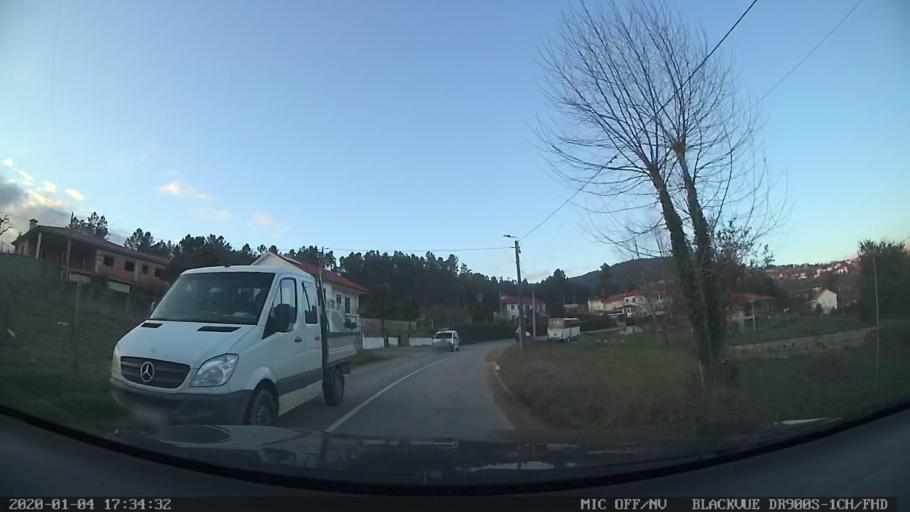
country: PT
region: Vila Real
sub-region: Mondim de Basto
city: Mondim de Basto
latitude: 41.4386
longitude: -7.9717
